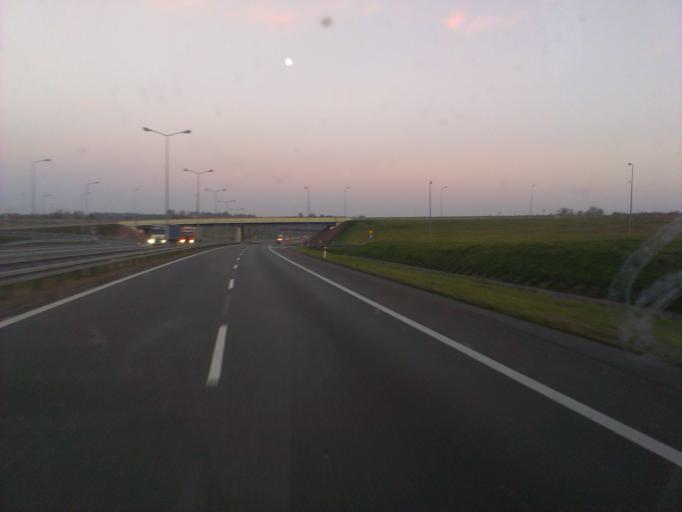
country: PL
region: Opole Voivodeship
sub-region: Powiat strzelecki
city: Ujazd
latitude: 50.4463
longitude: 18.3456
